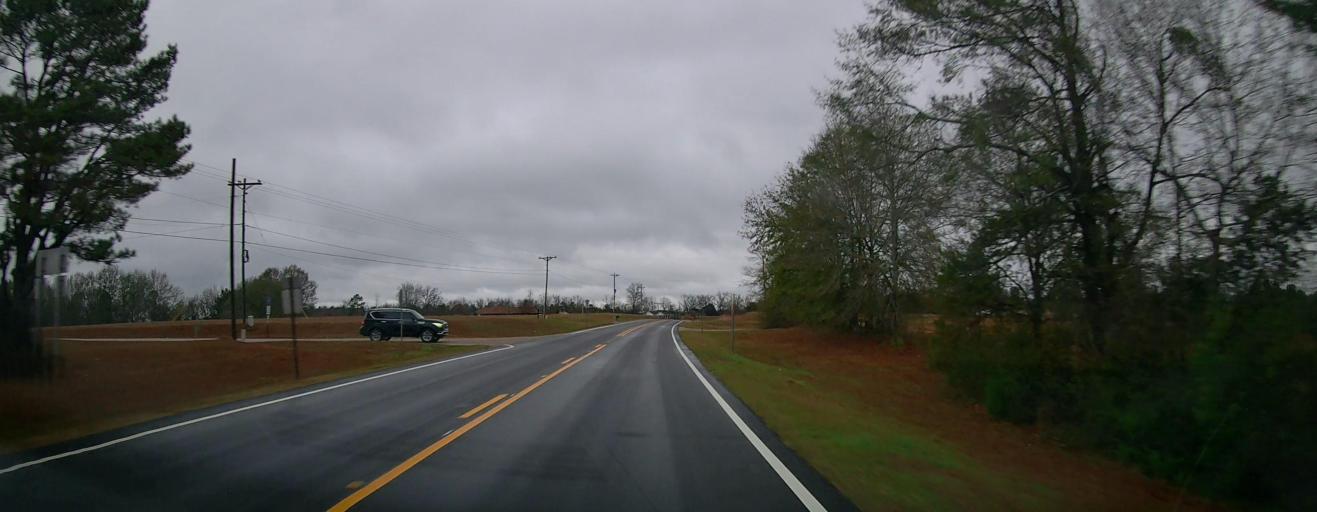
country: US
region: Alabama
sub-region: Chilton County
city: Thorsby
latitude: 32.7858
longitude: -86.9010
